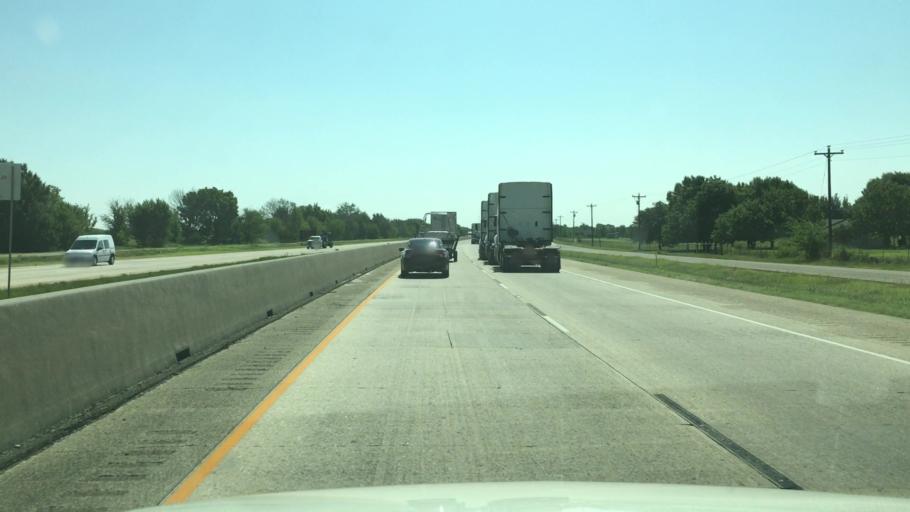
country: US
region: Texas
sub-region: Hunt County
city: Commerce
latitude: 33.1315
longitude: -95.7892
